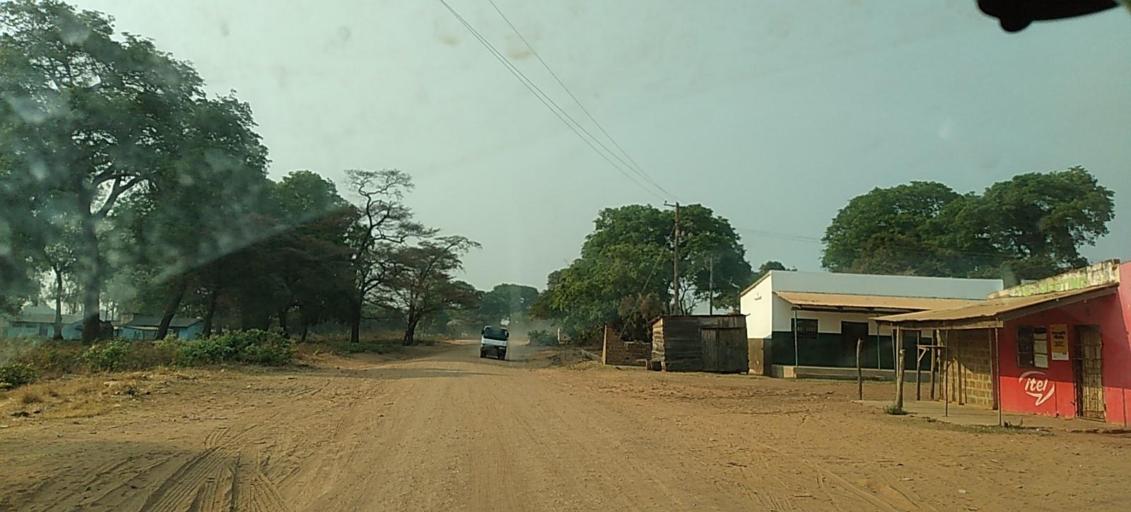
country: ZM
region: North-Western
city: Kabompo
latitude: -13.5936
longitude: 24.2027
